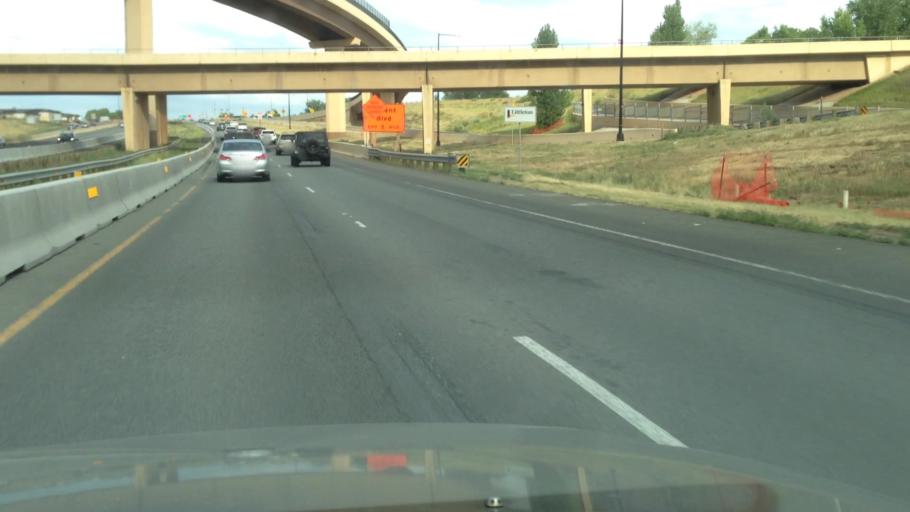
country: US
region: Colorado
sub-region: Arapahoe County
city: Columbine Valley
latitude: 39.5644
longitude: -105.0327
